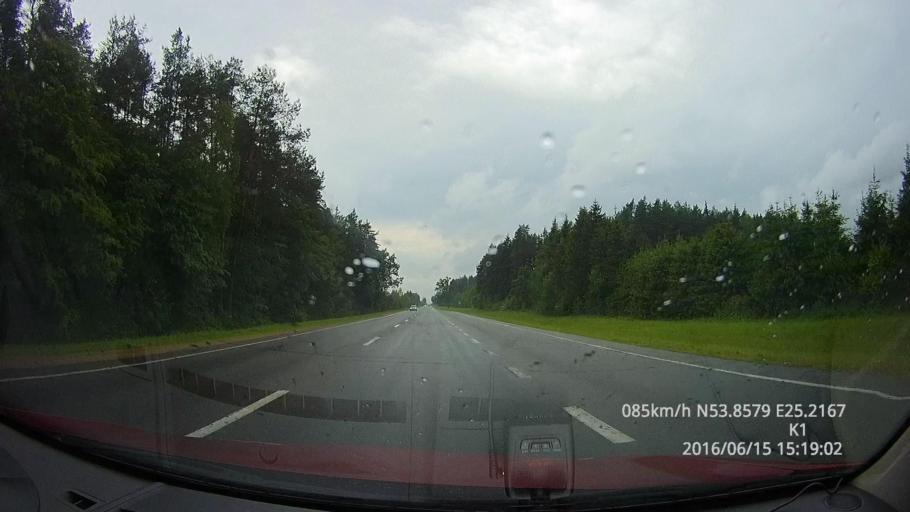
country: BY
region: Grodnenskaya
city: Lida
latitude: 53.8578
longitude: 25.2165
